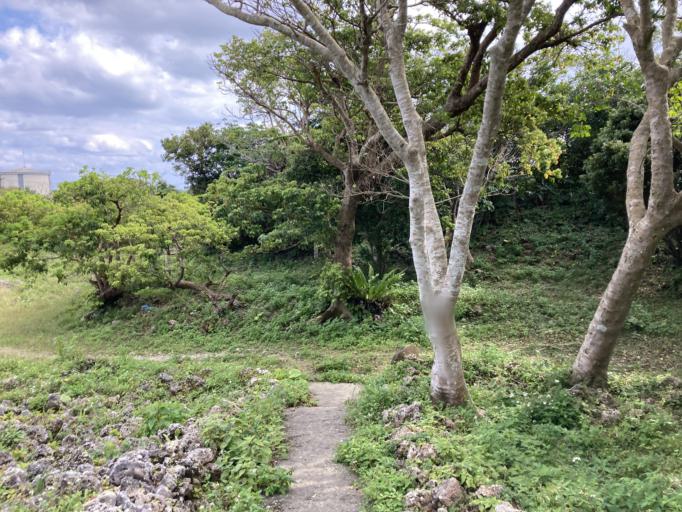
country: JP
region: Okinawa
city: Ginowan
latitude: 26.1865
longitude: 127.7599
